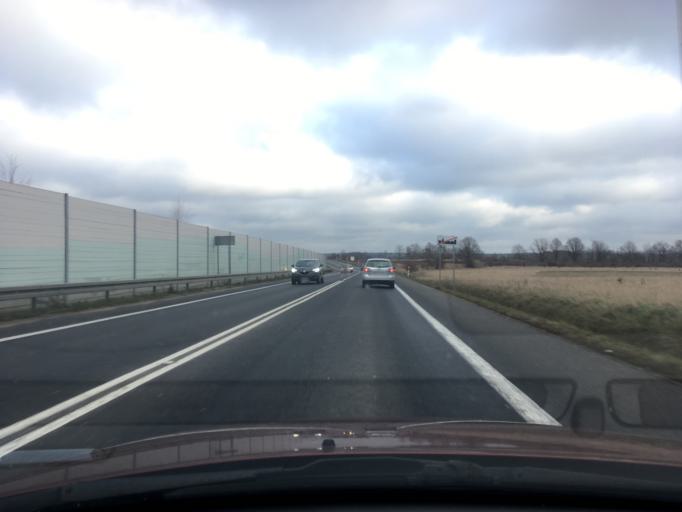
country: PL
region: Lower Silesian Voivodeship
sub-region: Powiat zgorzelecki
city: Zgorzelec
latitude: 51.1372
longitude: 15.0299
